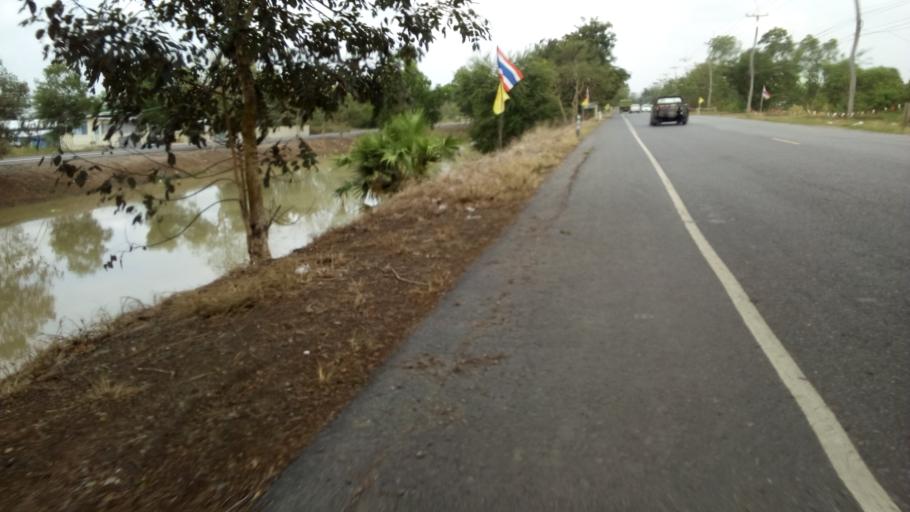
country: TH
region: Pathum Thani
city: Nong Suea
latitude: 14.2362
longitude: 100.8233
